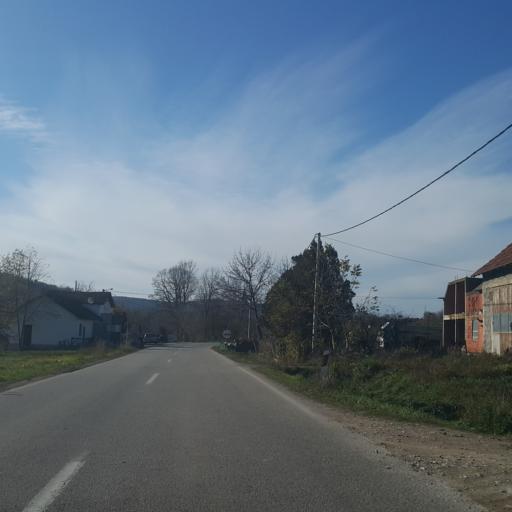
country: RS
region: Central Serbia
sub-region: Sumadijski Okrug
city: Topola
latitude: 44.2485
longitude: 20.7339
